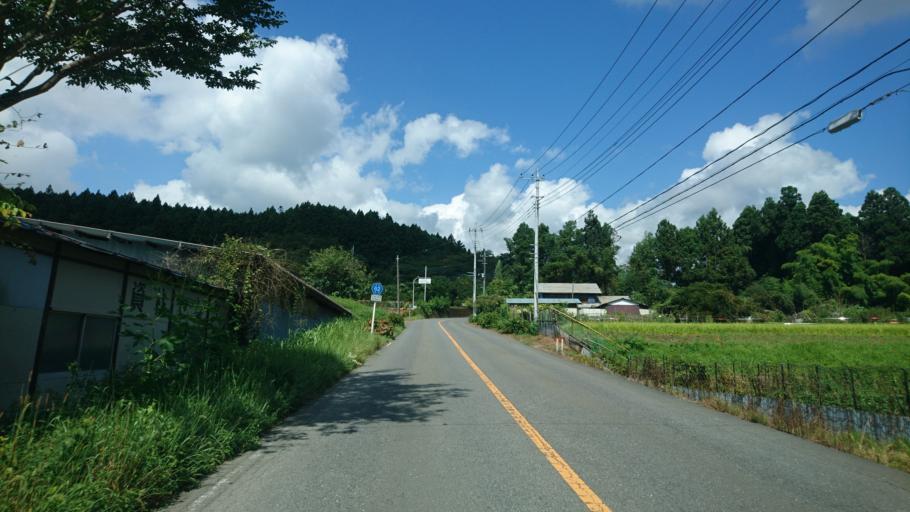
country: JP
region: Gunma
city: Omamacho-omama
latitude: 36.5028
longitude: 139.2640
